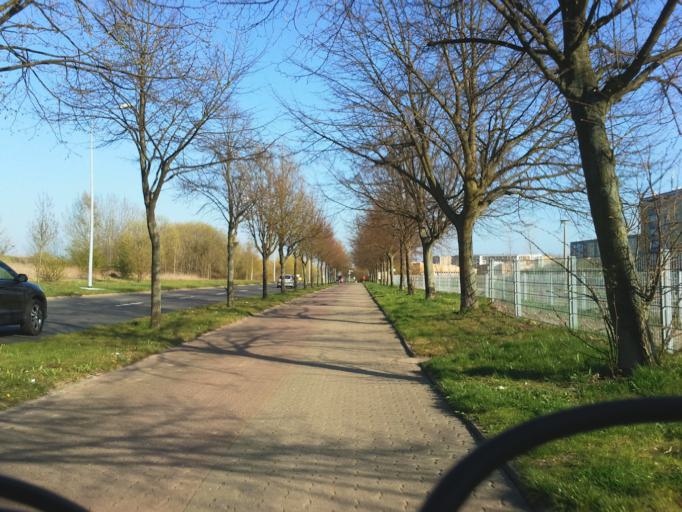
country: DE
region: Mecklenburg-Vorpommern
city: Dierkow-West
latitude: 54.1184
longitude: 12.1450
